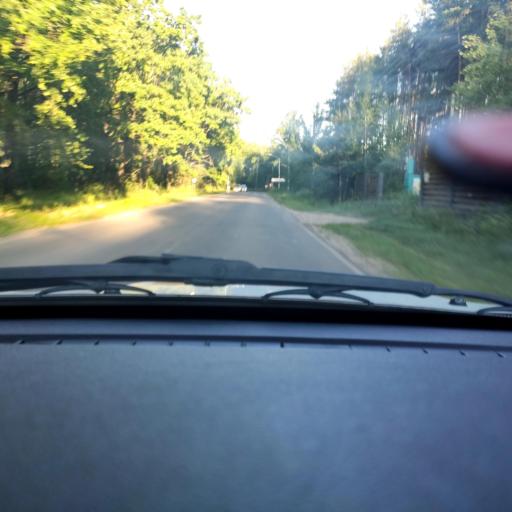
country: RU
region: Voronezj
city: Ramon'
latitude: 51.8945
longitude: 39.2791
